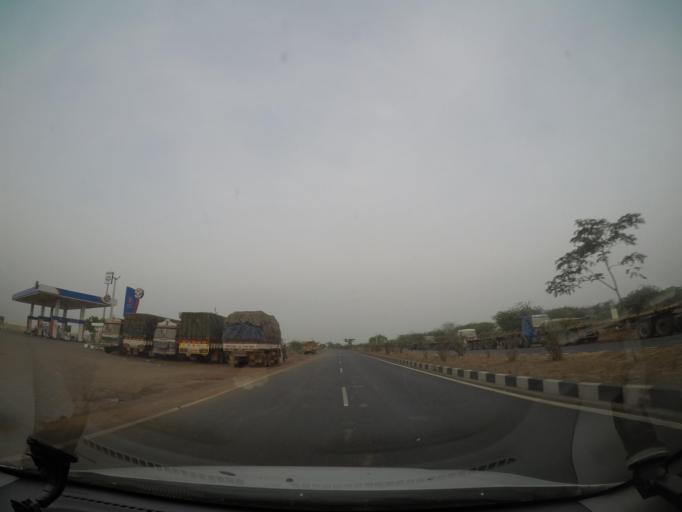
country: IN
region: Andhra Pradesh
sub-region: West Godavari
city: Eluru
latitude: 16.6317
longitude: 80.9522
